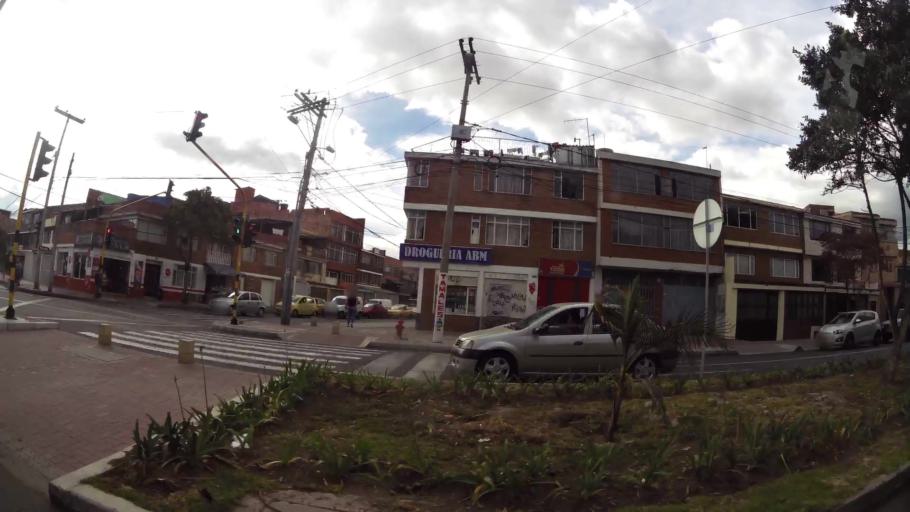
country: CO
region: Bogota D.C.
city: Bogota
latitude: 4.6076
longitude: -74.1374
